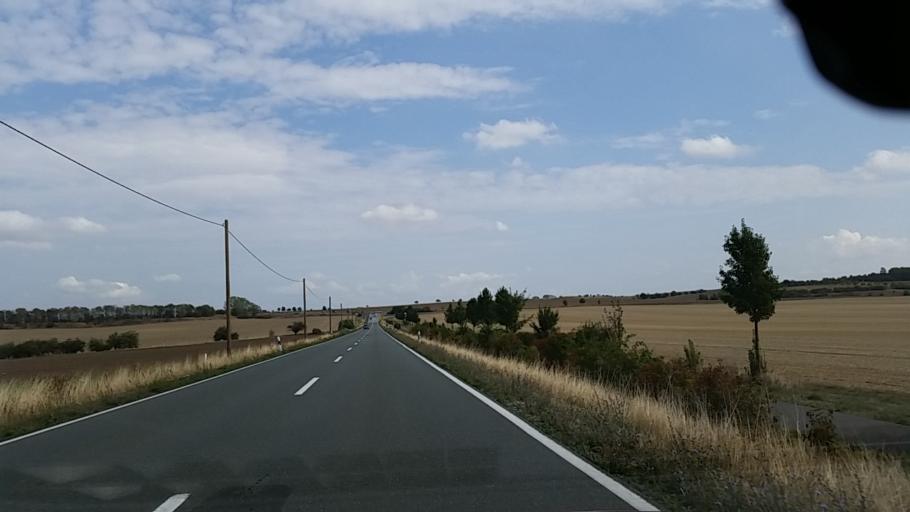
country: DE
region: Saxony-Anhalt
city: Querfurt
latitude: 51.3570
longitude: 11.5667
